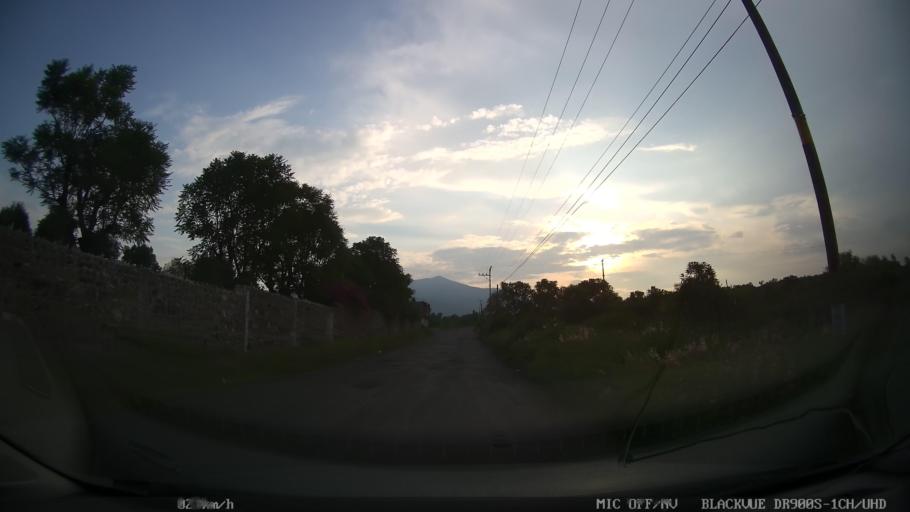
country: MX
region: Michoacan
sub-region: Morelia
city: La Mintzita (Piedra Dura)
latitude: 19.6487
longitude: -101.2899
